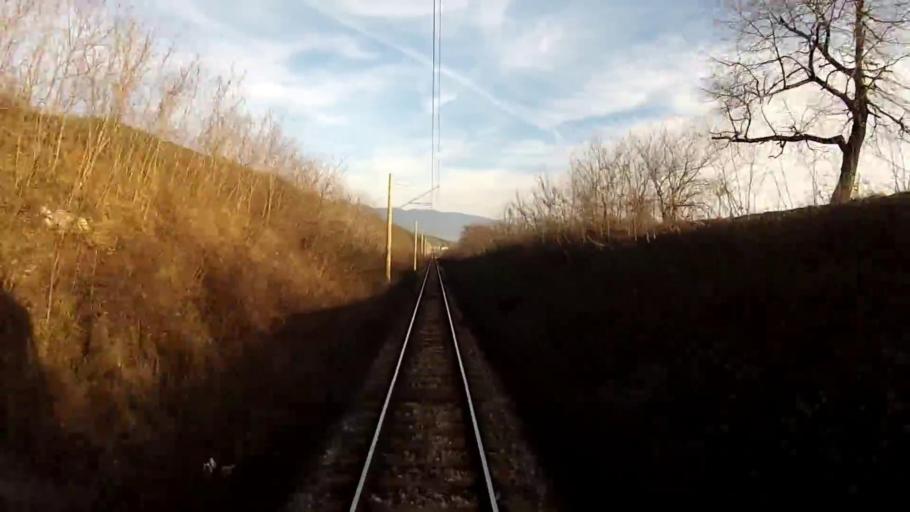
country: BG
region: Plovdiv
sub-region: Obshtina Karlovo
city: Klisura
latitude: 42.7186
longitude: 24.5832
